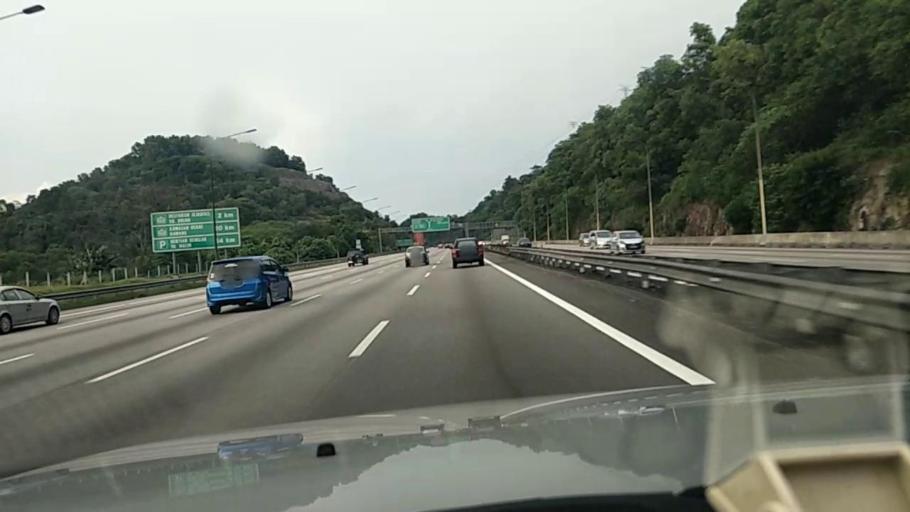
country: MY
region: Selangor
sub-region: Petaling
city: Petaling Jaya
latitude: 3.1698
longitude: 101.5980
